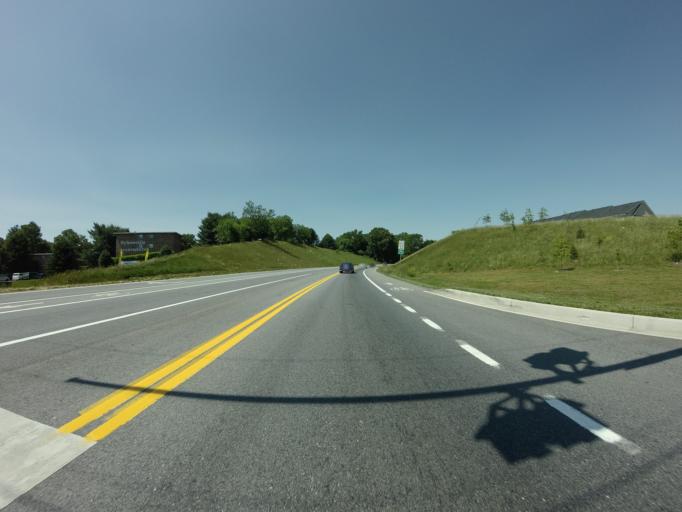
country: US
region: Maryland
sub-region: Carroll County
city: Sykesville
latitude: 39.3689
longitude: -76.9642
